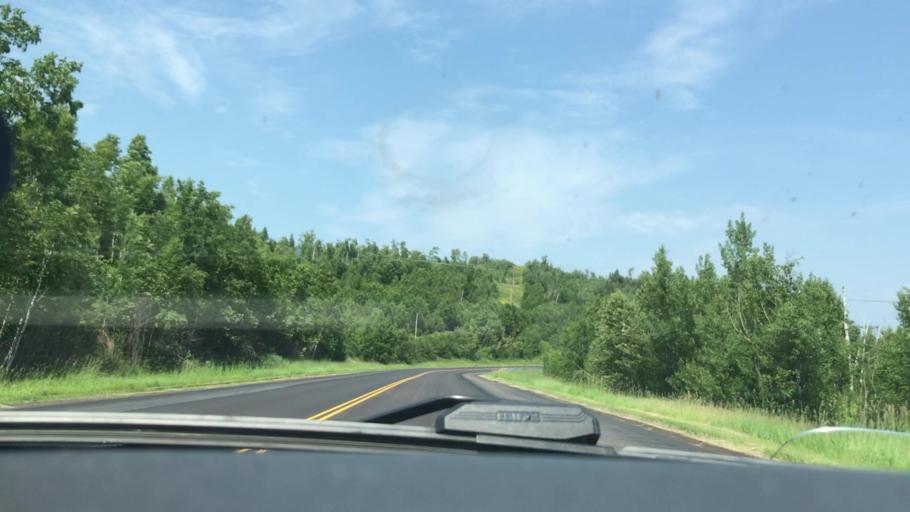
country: US
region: Minnesota
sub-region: Lake County
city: Silver Bay
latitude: 47.3650
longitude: -91.1726
